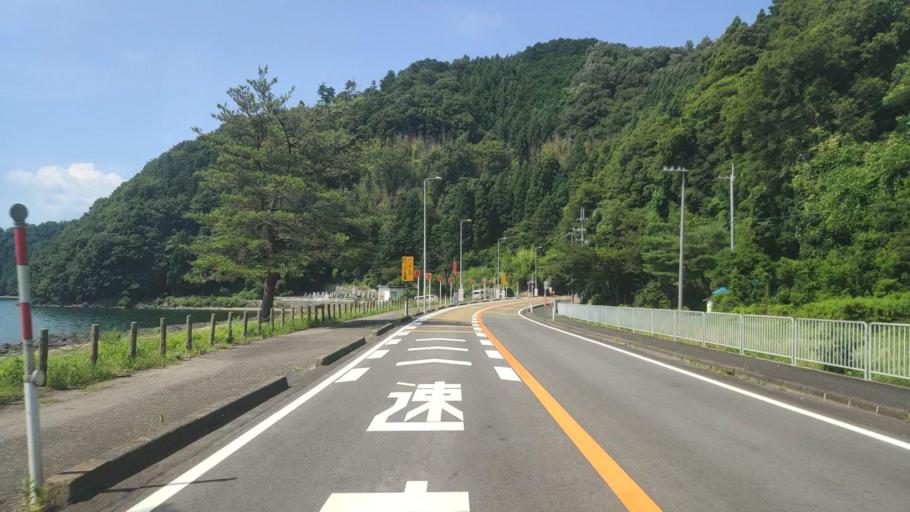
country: JP
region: Shiga Prefecture
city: Nagahama
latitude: 35.4577
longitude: 136.1986
